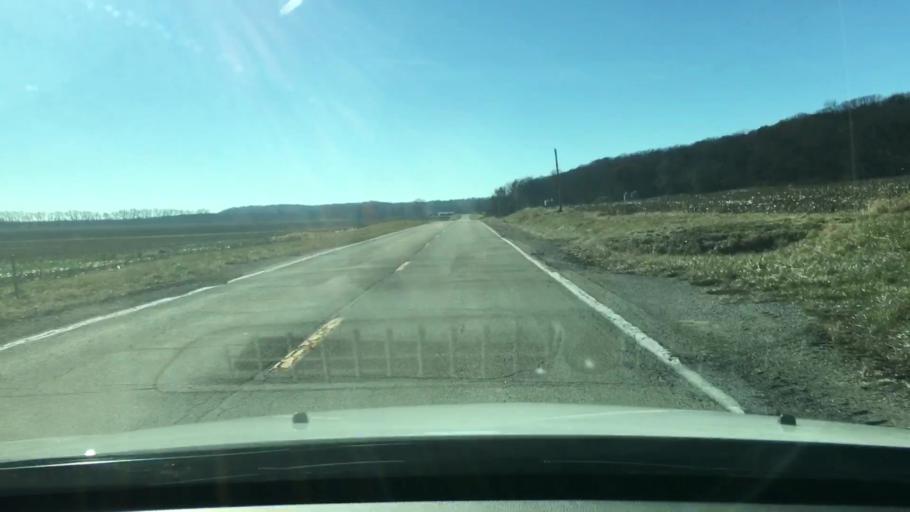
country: US
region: Illinois
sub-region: Mason County
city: Havana
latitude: 40.2426
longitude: -90.1906
